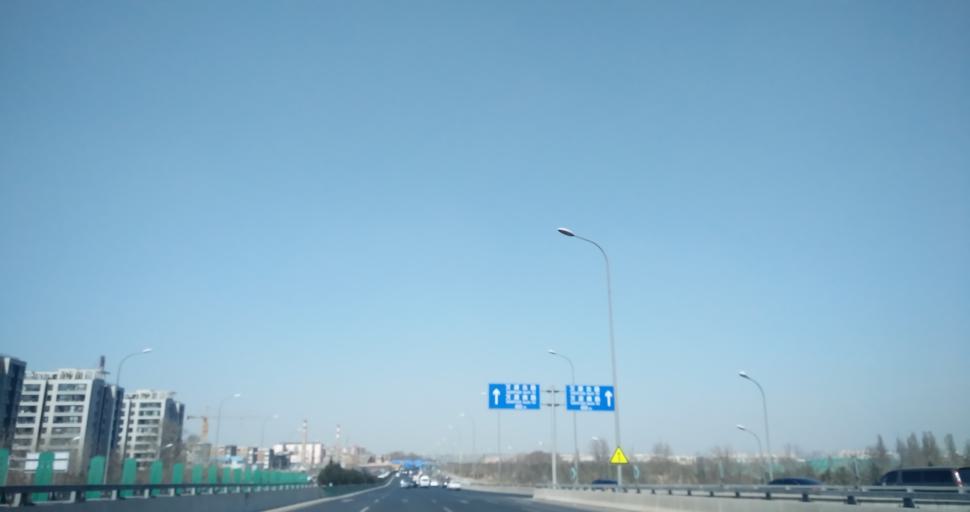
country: CN
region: Beijing
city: Jiugong
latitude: 39.7881
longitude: 116.4246
